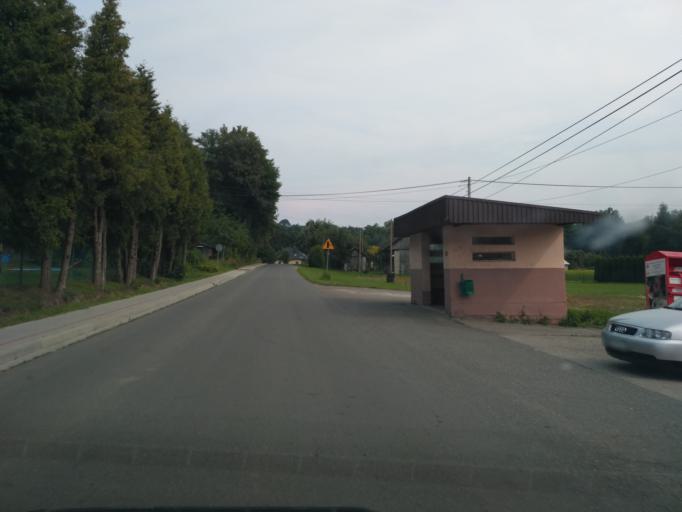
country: PL
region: Subcarpathian Voivodeship
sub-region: Powiat strzyzowski
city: Konieczkowa
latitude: 49.8420
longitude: 21.9255
